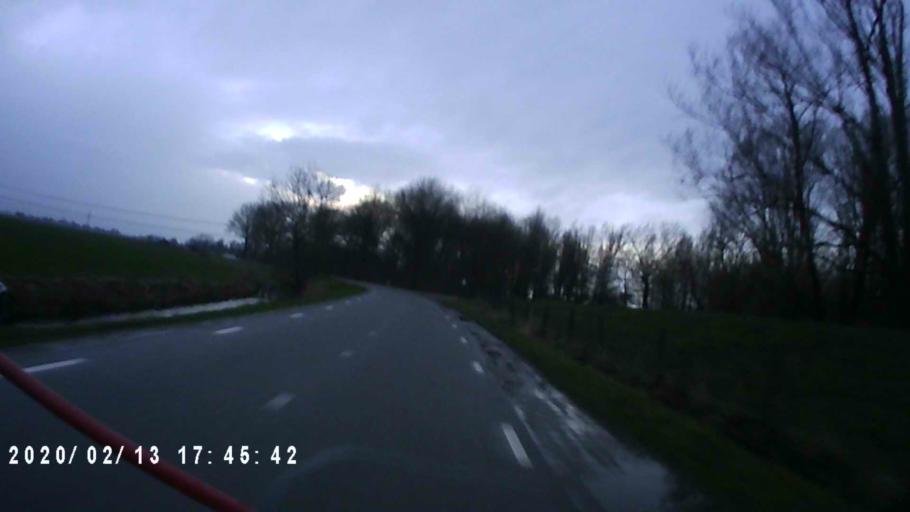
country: NL
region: Groningen
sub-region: Gemeente Zuidhorn
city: Aduard
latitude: 53.2300
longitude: 6.4770
